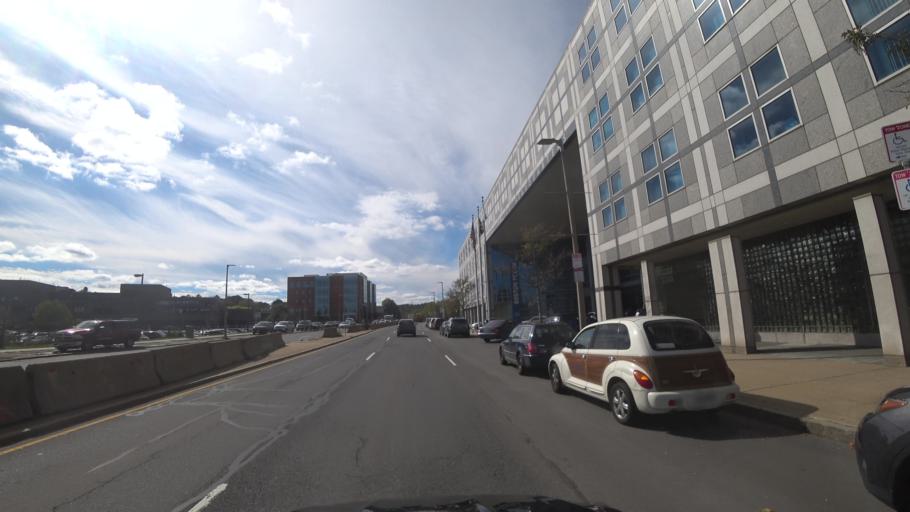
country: US
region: Massachusetts
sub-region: Norfolk County
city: Brookline
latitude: 42.3343
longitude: -71.0901
